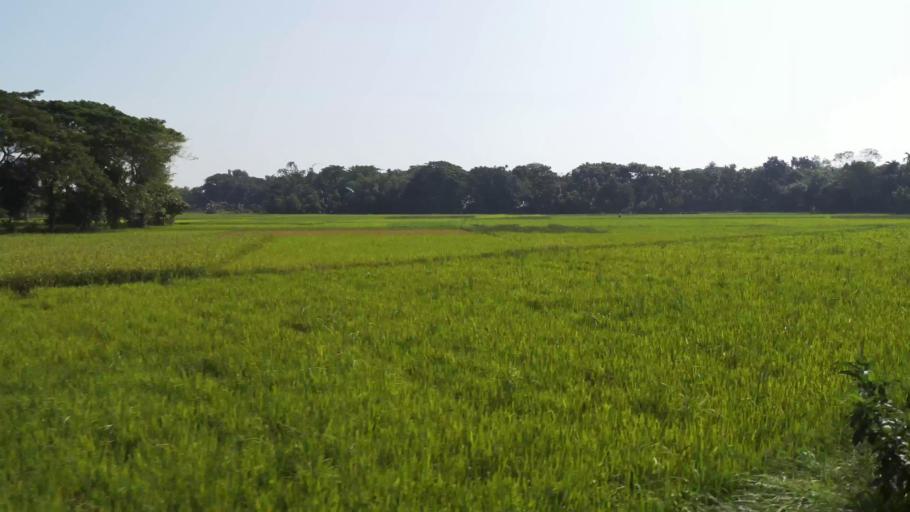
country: BD
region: Dhaka
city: Gafargaon
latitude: 24.5926
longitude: 90.5023
